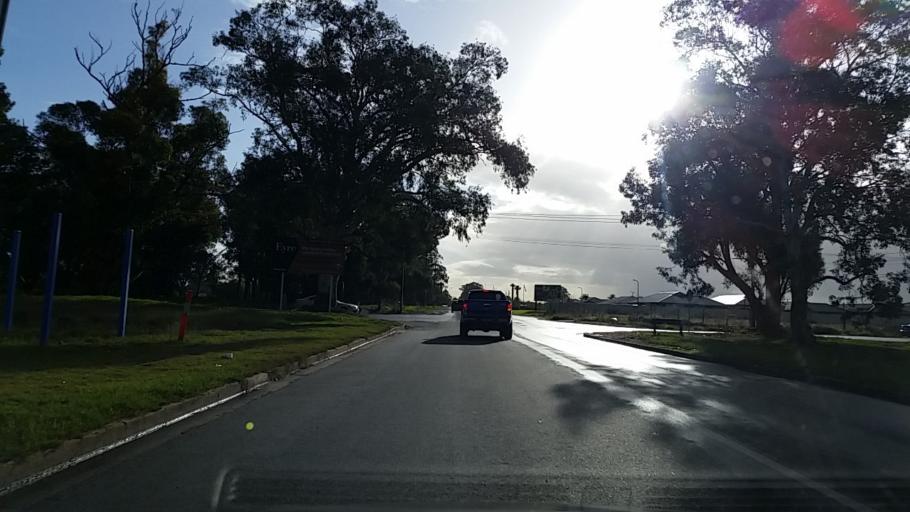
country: AU
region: South Australia
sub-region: Salisbury
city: Elizabeth
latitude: -34.6977
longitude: 138.6565
